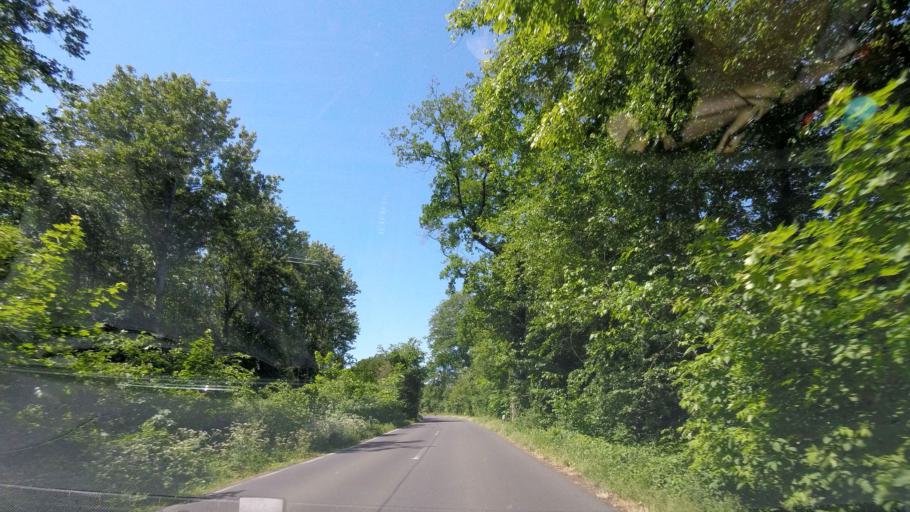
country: DE
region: Brandenburg
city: Potsdam
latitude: 52.3978
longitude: 13.0049
